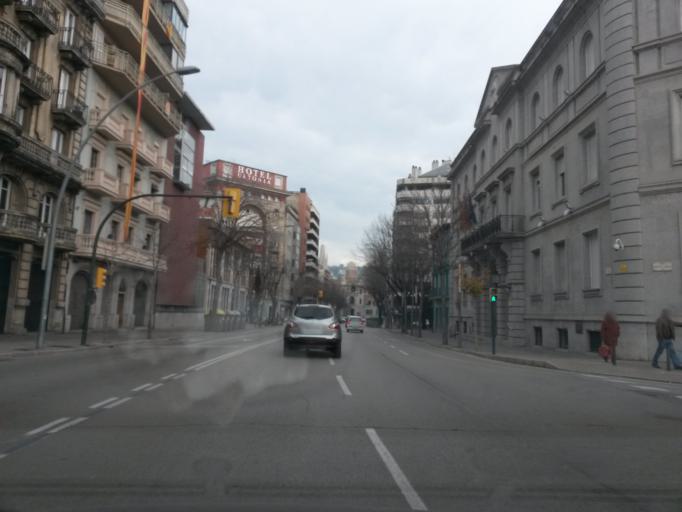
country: ES
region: Catalonia
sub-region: Provincia de Girona
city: Girona
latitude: 41.9844
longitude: 2.8206
